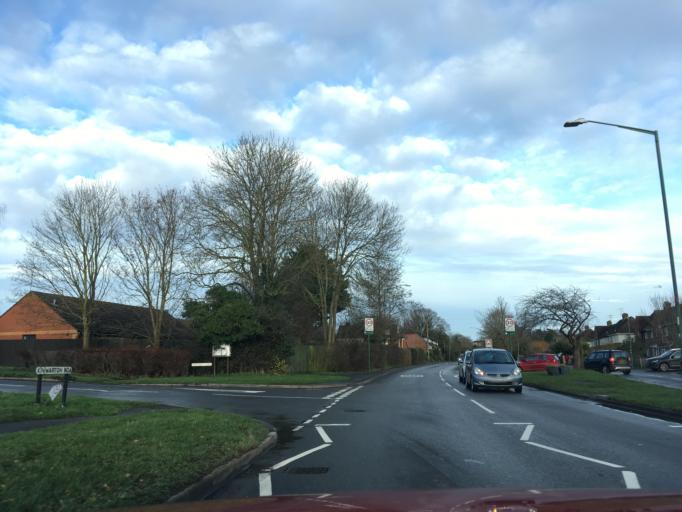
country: GB
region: England
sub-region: Warwickshire
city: Alcester
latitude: 52.2191
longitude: -1.8642
